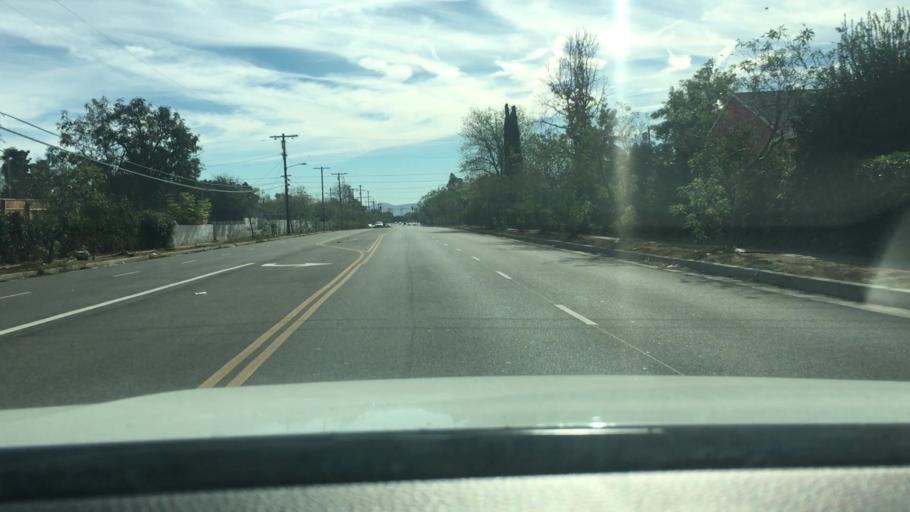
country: US
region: California
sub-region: Los Angeles County
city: San Fernando
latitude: 34.2352
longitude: -118.4189
